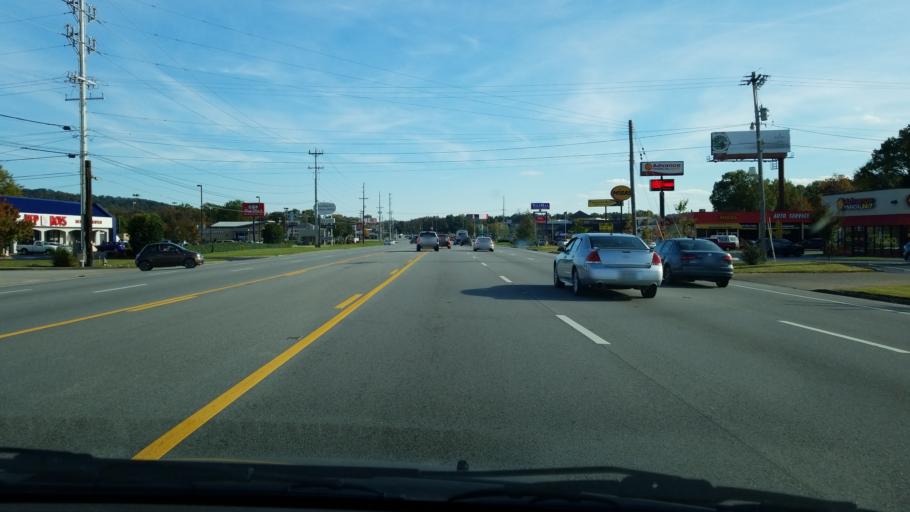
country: US
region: Tennessee
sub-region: Hamilton County
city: Red Bank
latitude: 35.1261
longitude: -85.2415
